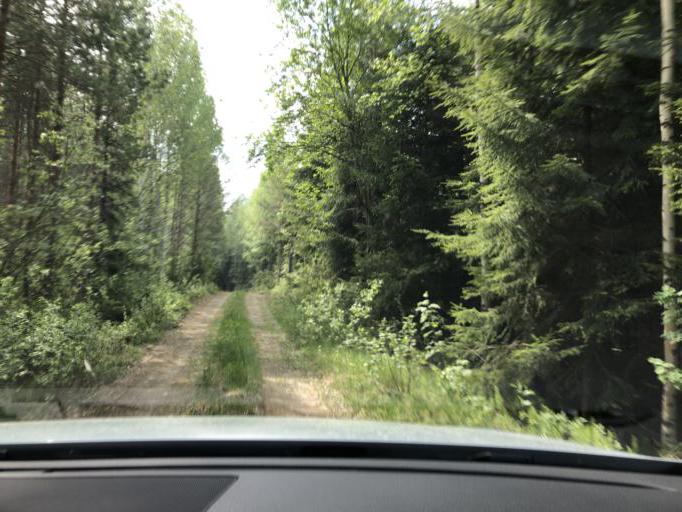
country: SE
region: Dalarna
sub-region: Avesta Kommun
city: Horndal
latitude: 60.2237
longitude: 16.5136
